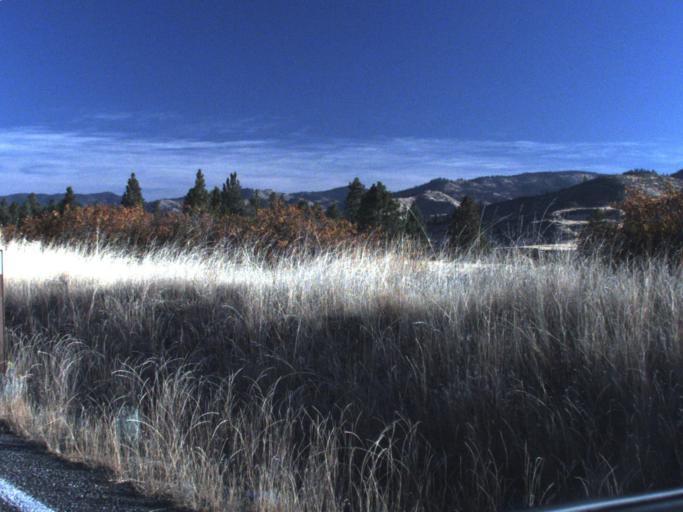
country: US
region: Washington
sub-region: Okanogan County
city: Coulee Dam
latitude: 47.9890
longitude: -118.6931
